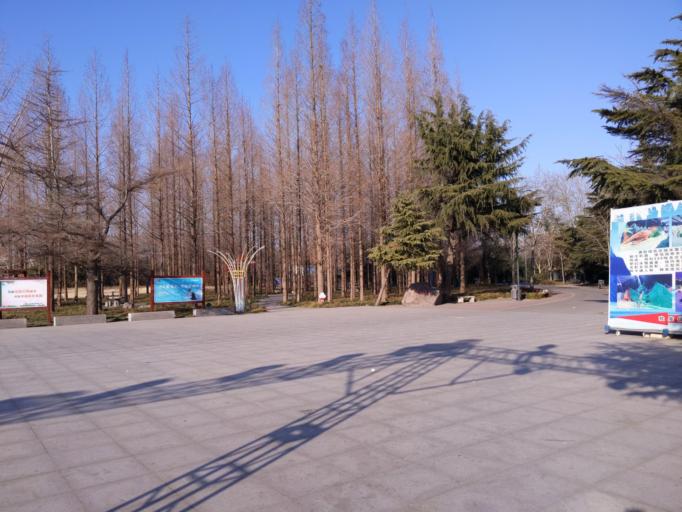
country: CN
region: Henan Sheng
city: Puyang
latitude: 35.7750
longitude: 114.9617
